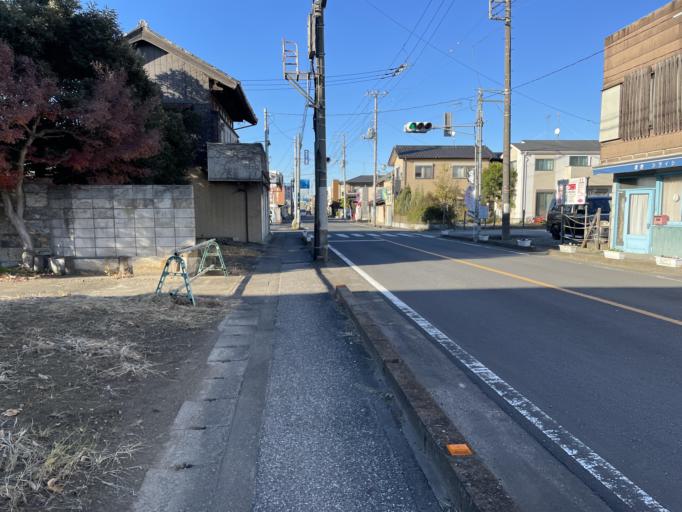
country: JP
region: Saitama
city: Kurihashi
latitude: 36.1385
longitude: 139.7038
